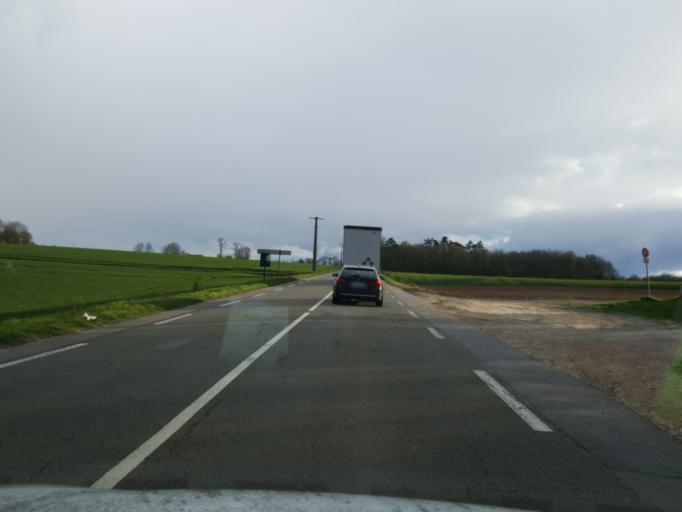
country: FR
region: Ile-de-France
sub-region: Departement des Yvelines
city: Limay
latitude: 49.0254
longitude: 1.7440
